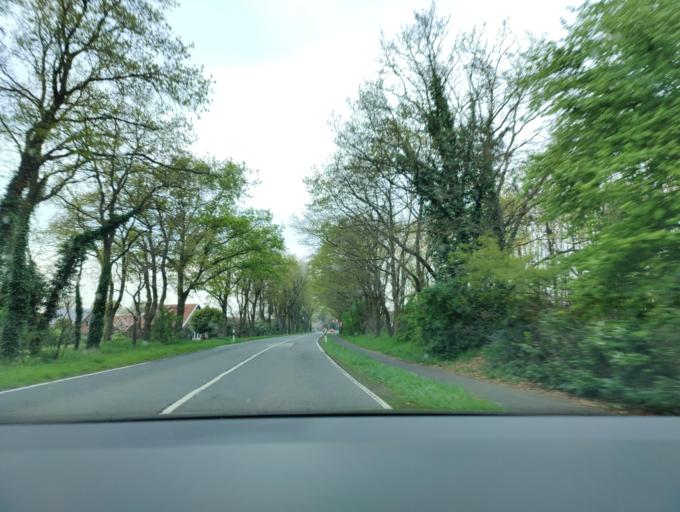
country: DE
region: Lower Saxony
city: Wietmarschen
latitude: 52.5107
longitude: 7.1443
